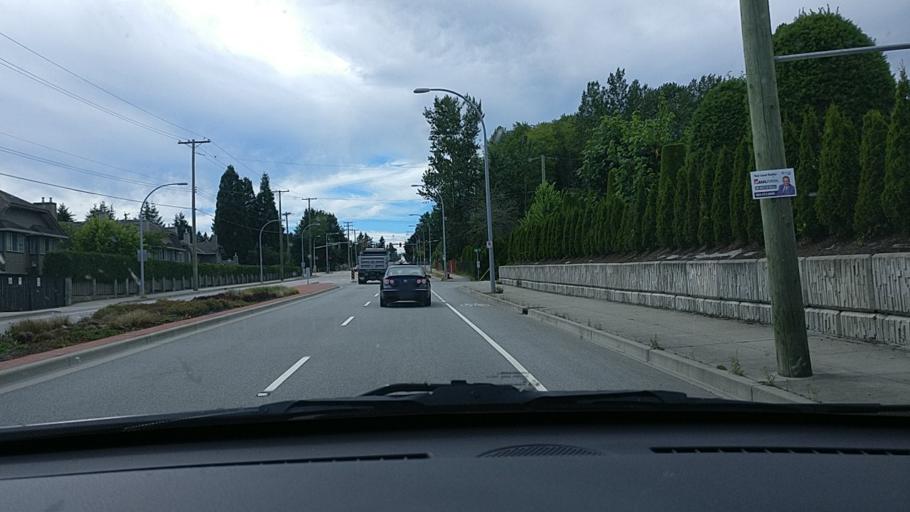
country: CA
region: British Columbia
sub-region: Greater Vancouver Regional District
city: White Rock
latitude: 49.0311
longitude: -122.7730
